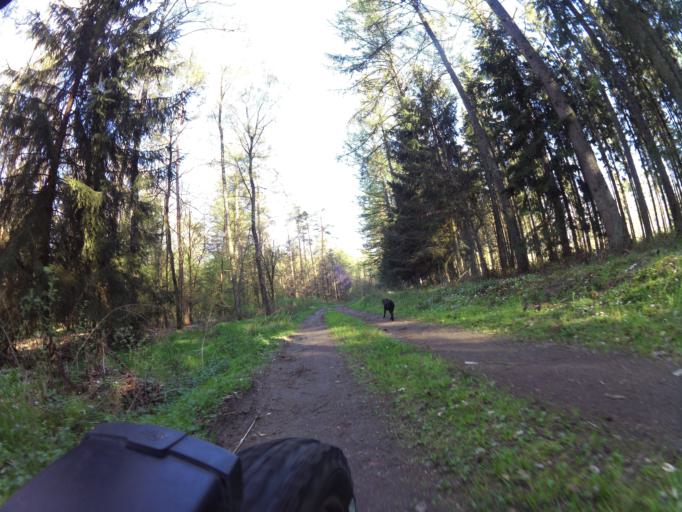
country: PL
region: West Pomeranian Voivodeship
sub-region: Powiat lobeski
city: Lobez
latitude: 53.7453
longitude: 15.6214
